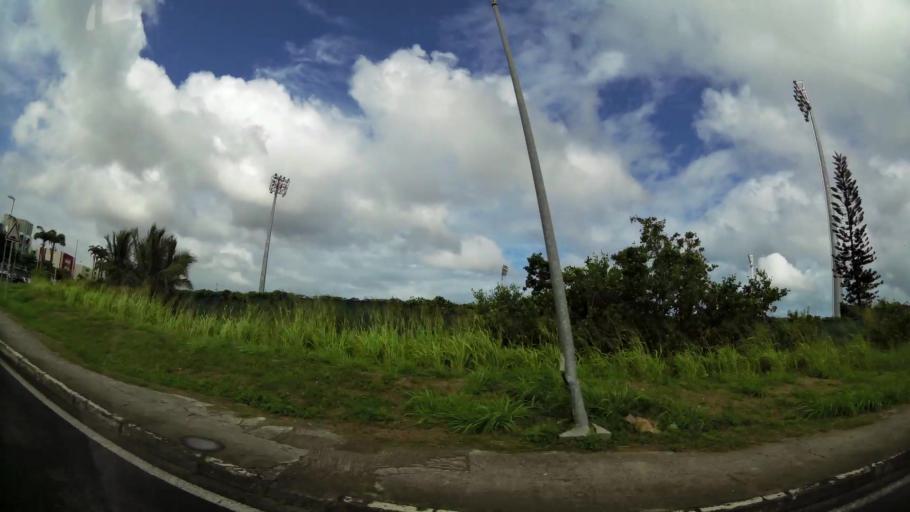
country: GP
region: Guadeloupe
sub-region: Guadeloupe
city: Pointe-a-Pitre
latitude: 16.2507
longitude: -61.5423
